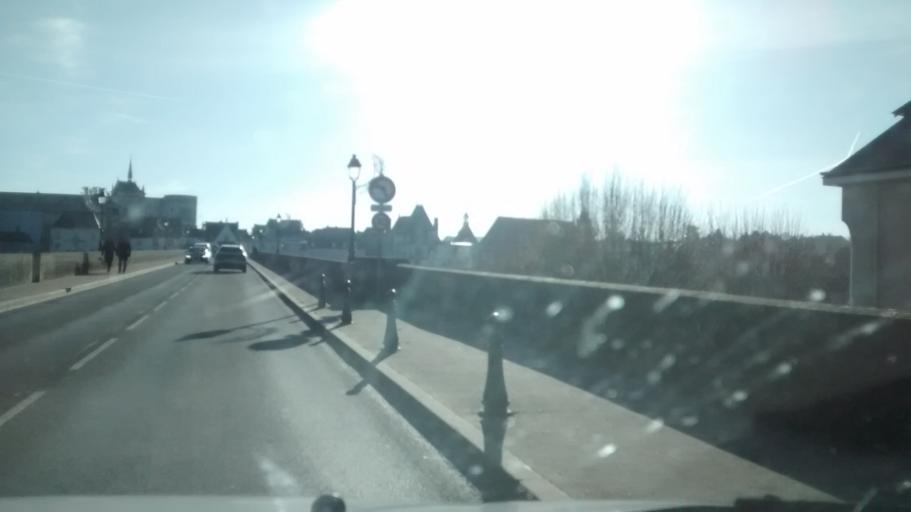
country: FR
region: Centre
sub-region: Departement d'Indre-et-Loire
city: Amboise
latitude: 47.4157
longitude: 0.9829
